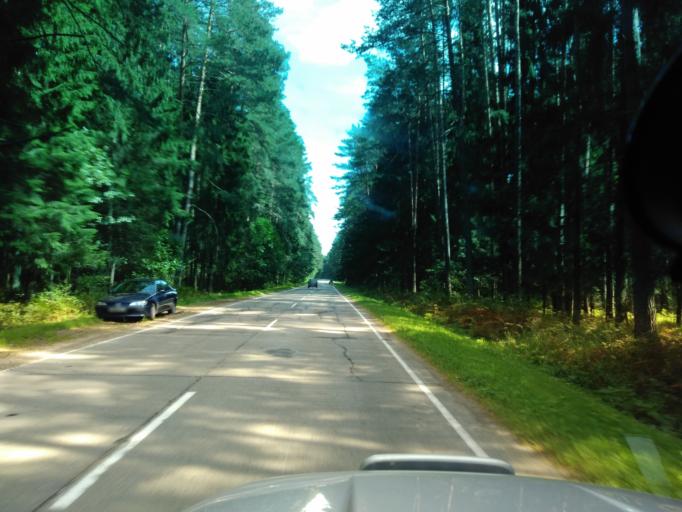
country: BY
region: Minsk
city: Stan'kava
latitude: 53.6220
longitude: 27.3023
